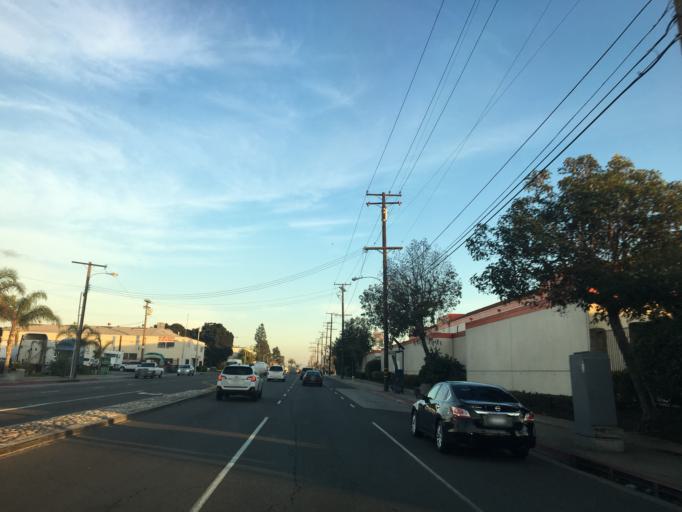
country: US
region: California
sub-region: Los Angeles County
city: Montebello
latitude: 33.9969
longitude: -118.1237
